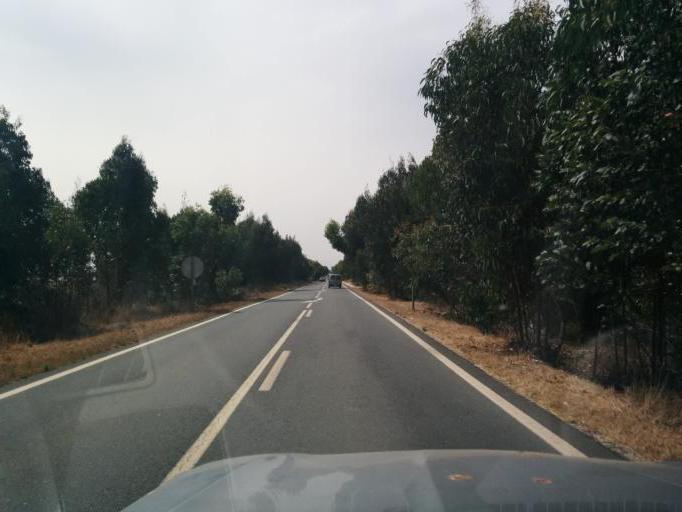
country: PT
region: Beja
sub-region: Odemira
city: Vila Nova de Milfontes
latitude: 37.6690
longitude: -8.7595
